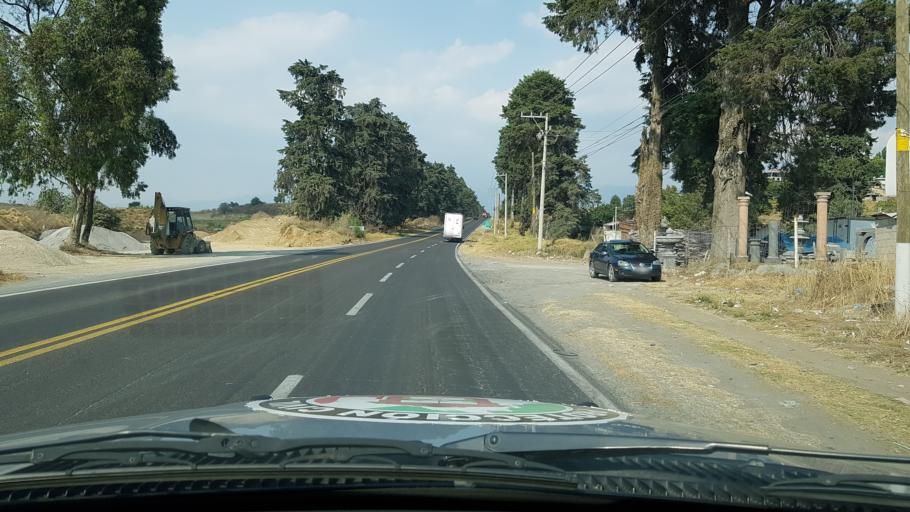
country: MX
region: Mexico
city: Ozumba de Alzate
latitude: 19.0386
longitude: -98.8065
